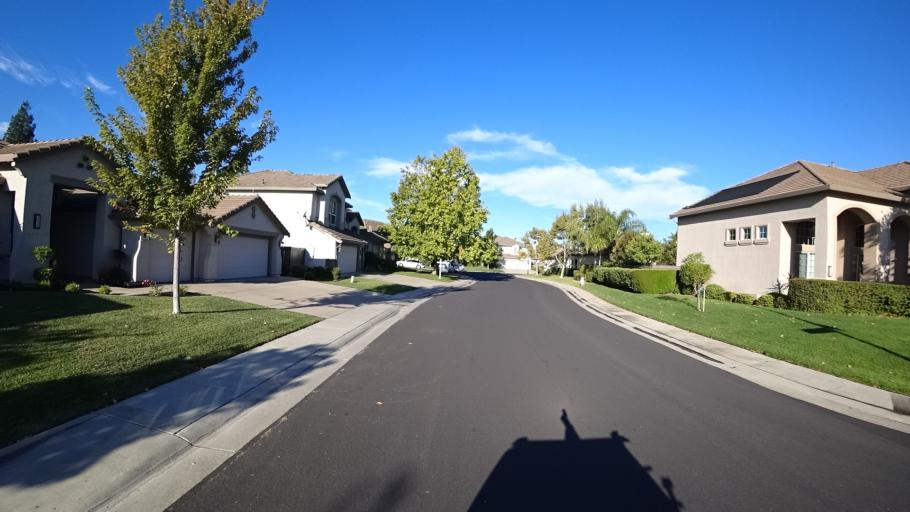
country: US
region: California
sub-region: Sacramento County
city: Laguna
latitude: 38.3985
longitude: -121.4736
